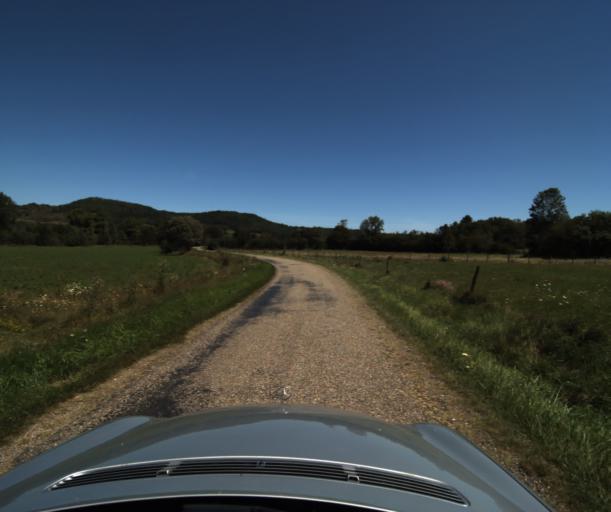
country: FR
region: Languedoc-Roussillon
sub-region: Departement de l'Aude
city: Chalabre
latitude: 42.9921
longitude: 1.9241
